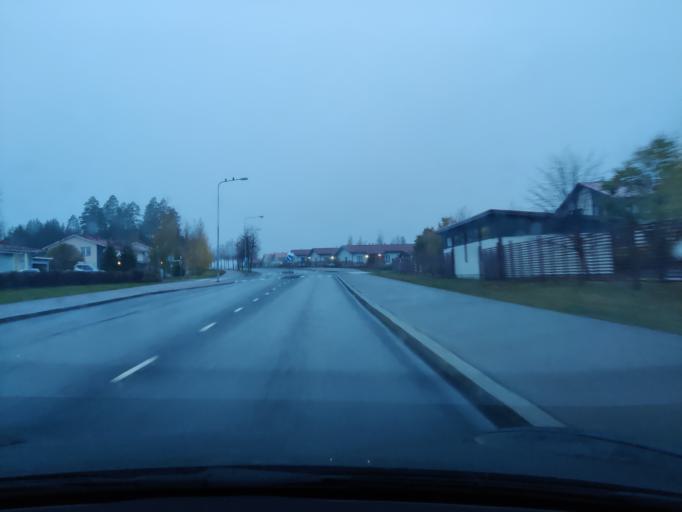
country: FI
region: Northern Savo
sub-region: Kuopio
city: Kuopio
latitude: 62.8264
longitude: 27.6879
